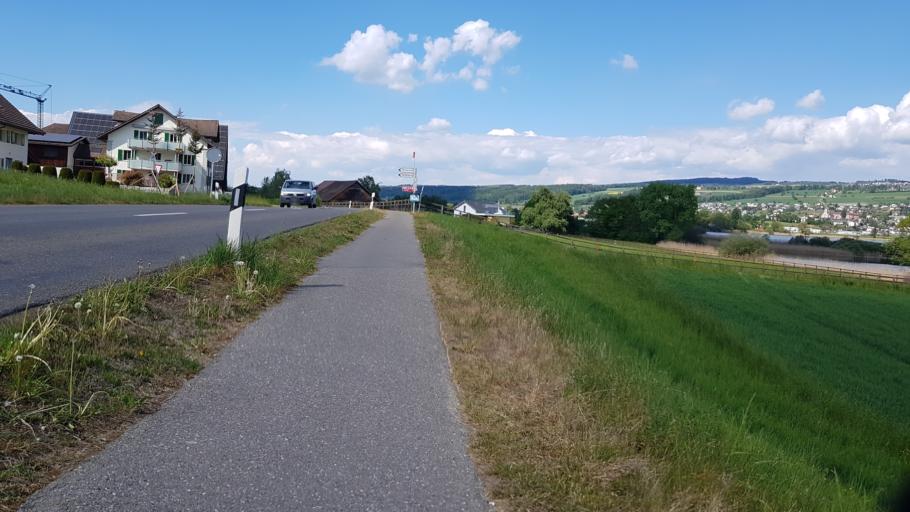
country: CH
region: Lucerne
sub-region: Hochdorf District
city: Hitzkirch
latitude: 47.2093
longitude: 8.2424
